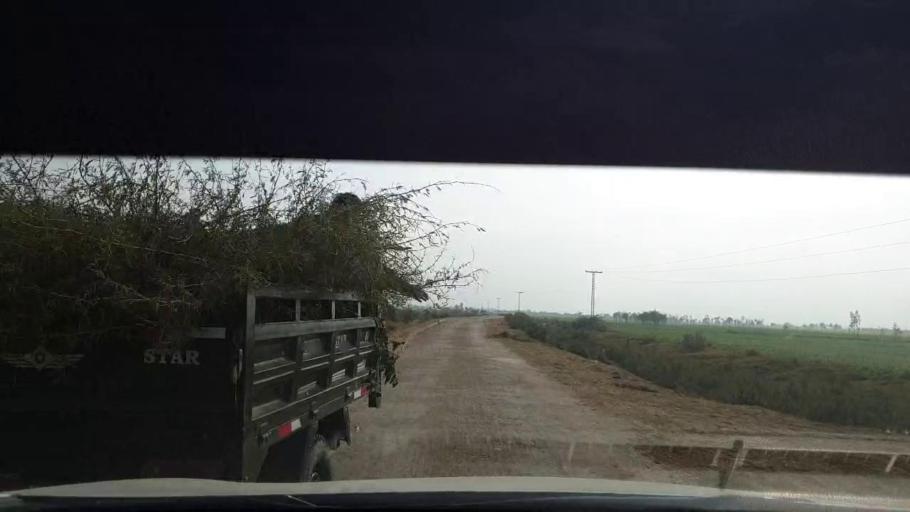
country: PK
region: Sindh
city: Berani
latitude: 25.7759
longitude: 68.8758
